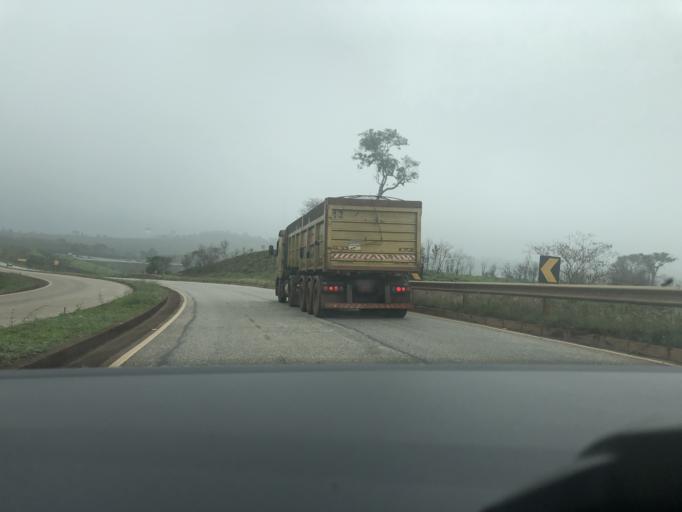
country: BR
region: Minas Gerais
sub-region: Congonhas
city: Congonhas
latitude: -20.5920
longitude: -43.9540
